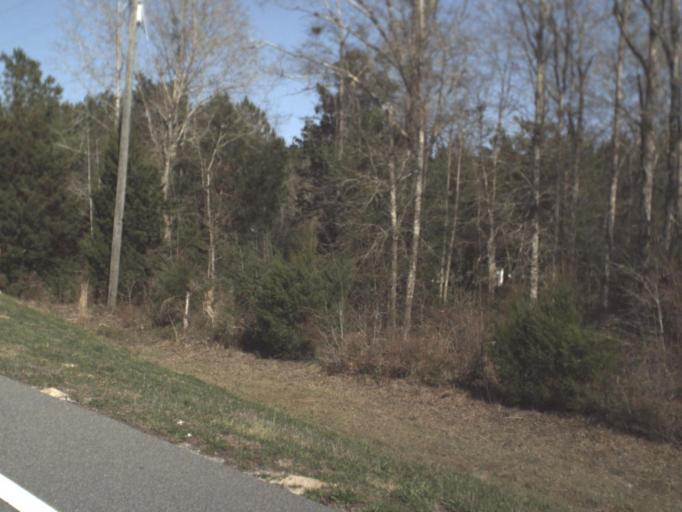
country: US
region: Florida
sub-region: Calhoun County
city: Blountstown
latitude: 30.3340
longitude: -85.2210
